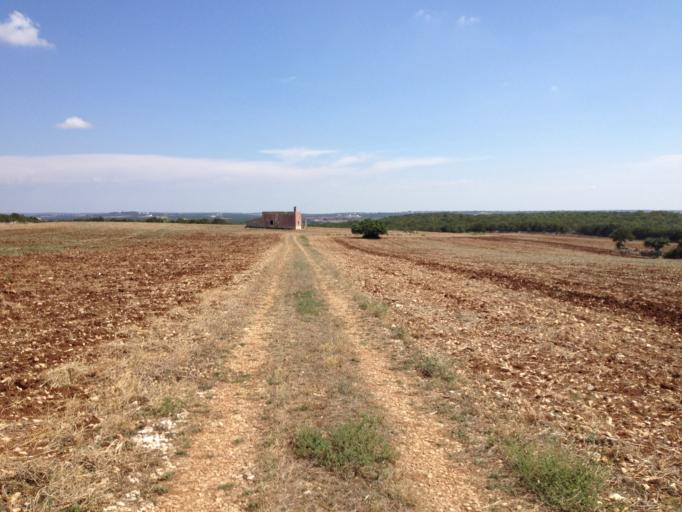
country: IT
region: Apulia
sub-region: Provincia di Bari
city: Gioia del Colle
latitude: 40.8242
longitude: 16.9967
